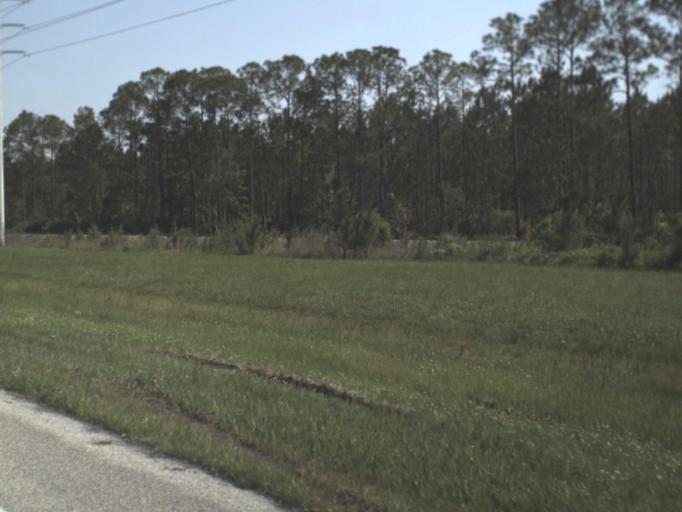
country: US
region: Florida
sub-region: Saint Johns County
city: Palm Valley
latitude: 30.0722
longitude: -81.4462
